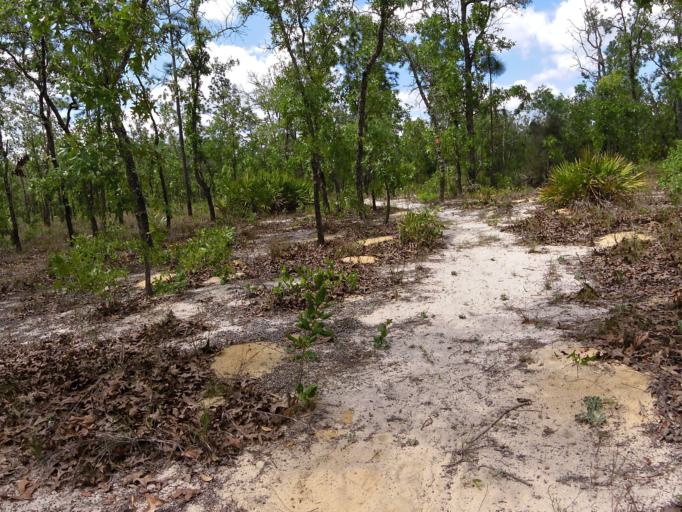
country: US
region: Florida
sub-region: Clay County
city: Keystone Heights
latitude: 29.8375
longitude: -81.9631
